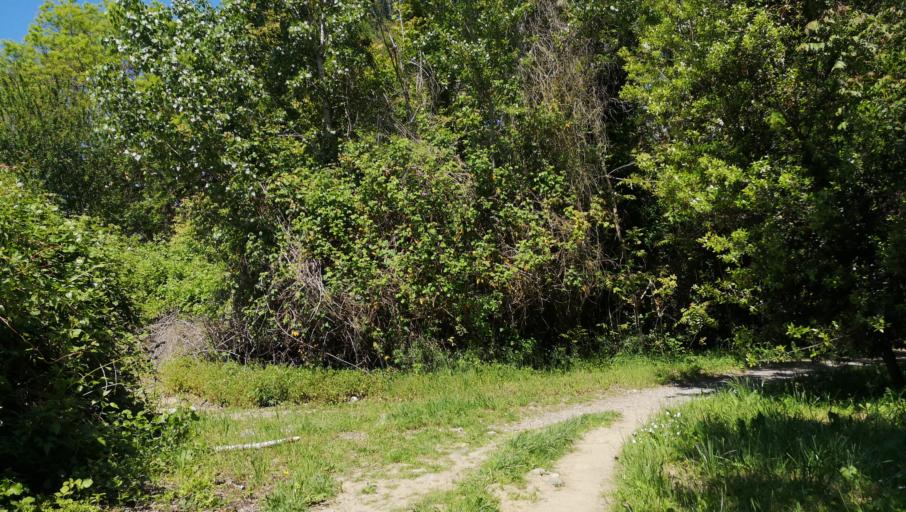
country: FR
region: Midi-Pyrenees
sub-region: Departement de la Haute-Garonne
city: Beauzelle
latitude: 43.6539
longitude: 1.3885
